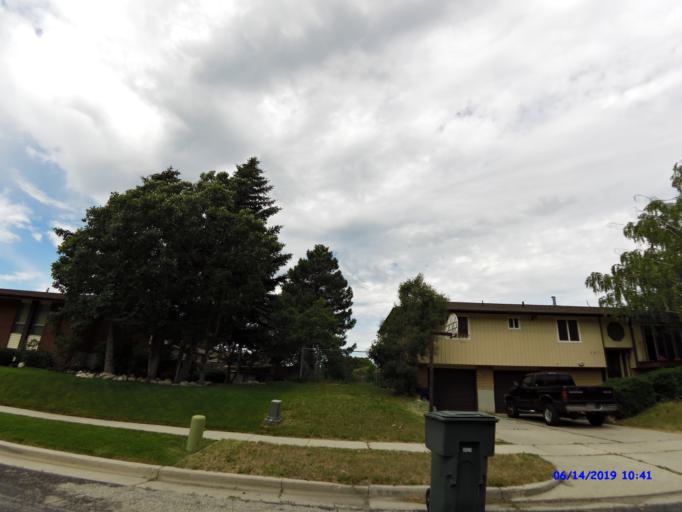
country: US
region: Utah
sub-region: Weber County
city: Ogden
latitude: 41.2383
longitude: -111.9422
